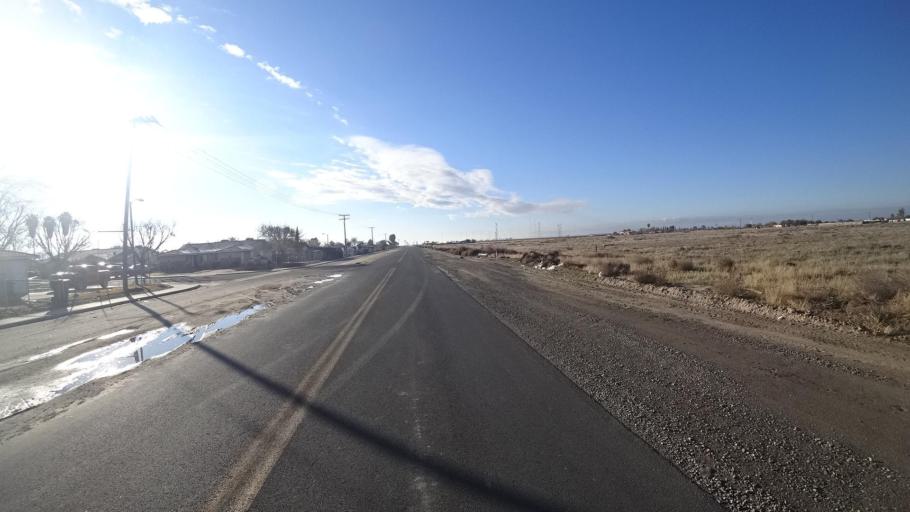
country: US
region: California
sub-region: Kern County
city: Delano
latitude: 35.7741
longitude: -119.2764
